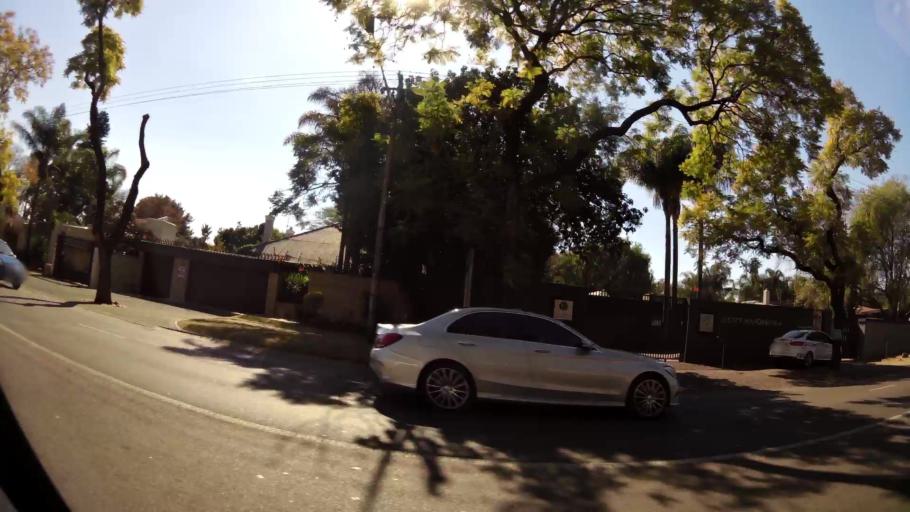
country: ZA
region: Gauteng
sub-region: City of Tshwane Metropolitan Municipality
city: Pretoria
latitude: -25.7673
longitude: 28.2373
